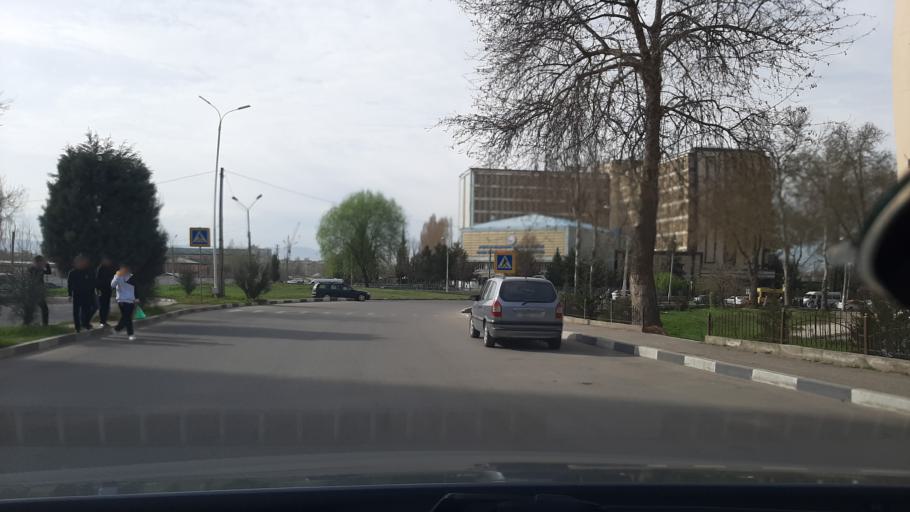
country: TJ
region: Dushanbe
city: Dushanbe
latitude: 38.5782
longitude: 68.7490
